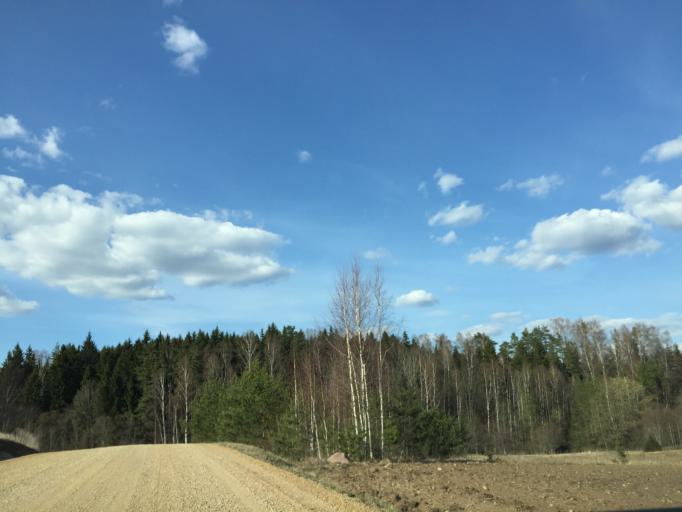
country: EE
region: Tartu
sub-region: Elva linn
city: Elva
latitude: 58.0973
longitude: 26.5084
